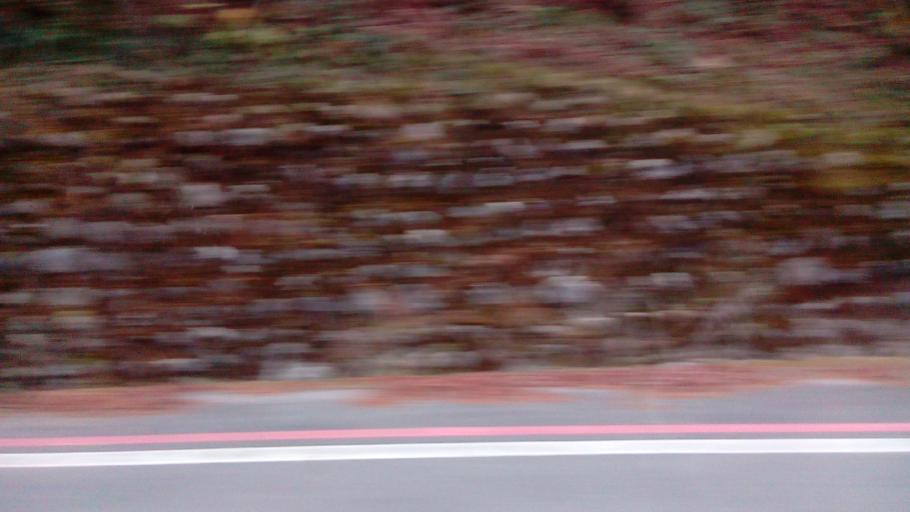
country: TW
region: Taiwan
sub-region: Hualien
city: Hualian
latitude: 24.3774
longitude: 121.3379
